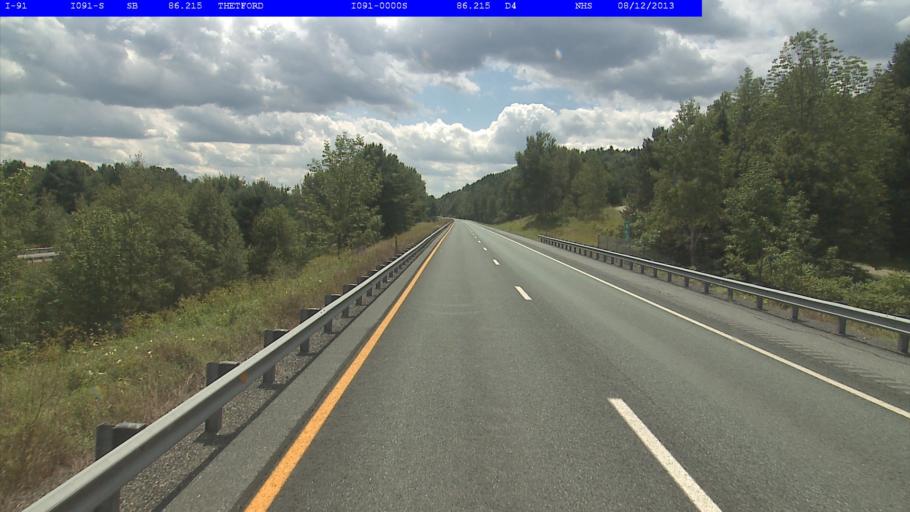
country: US
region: New Hampshire
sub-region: Grafton County
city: Lyme
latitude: 43.8398
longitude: -72.2028
